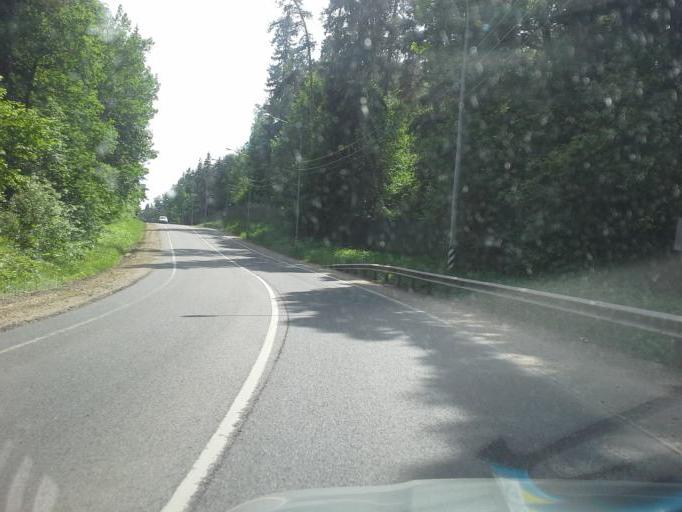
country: RU
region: Moskovskaya
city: Gorki Vtoryye
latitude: 55.7135
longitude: 37.1660
